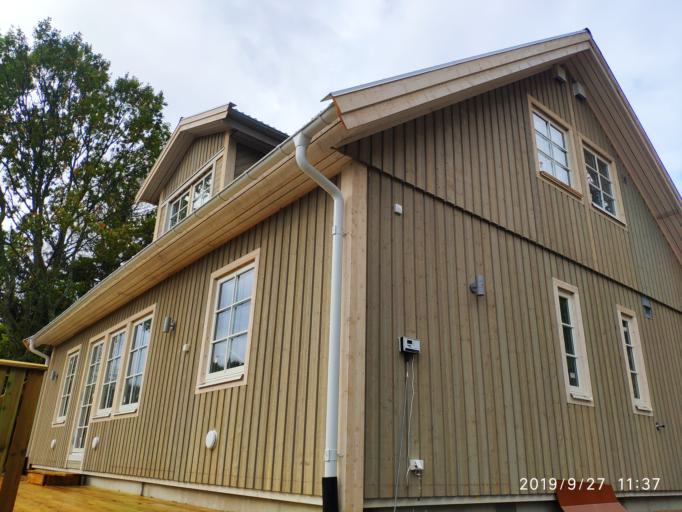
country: NO
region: Rogaland
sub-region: Karmoy
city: Kopervik
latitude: 59.2897
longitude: 5.3631
